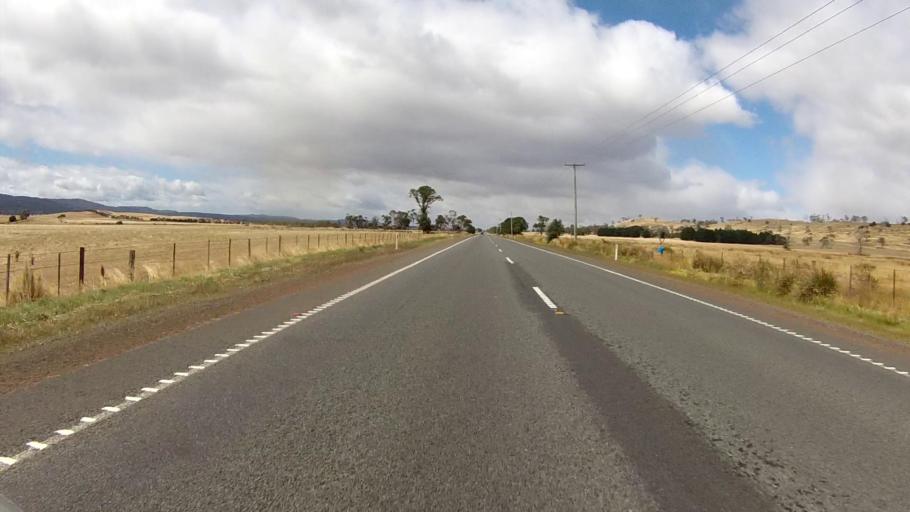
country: AU
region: Tasmania
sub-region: Northern Midlands
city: Evandale
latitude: -41.9594
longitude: 147.4978
